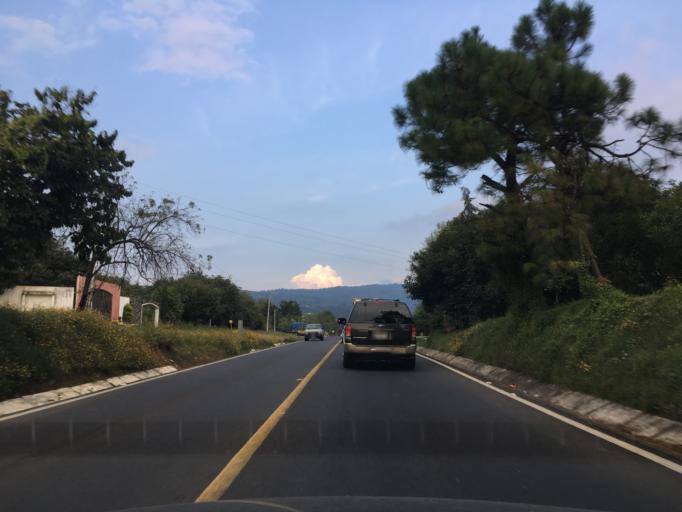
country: MX
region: Michoacan
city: Tingambato
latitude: 19.4999
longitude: -101.8698
